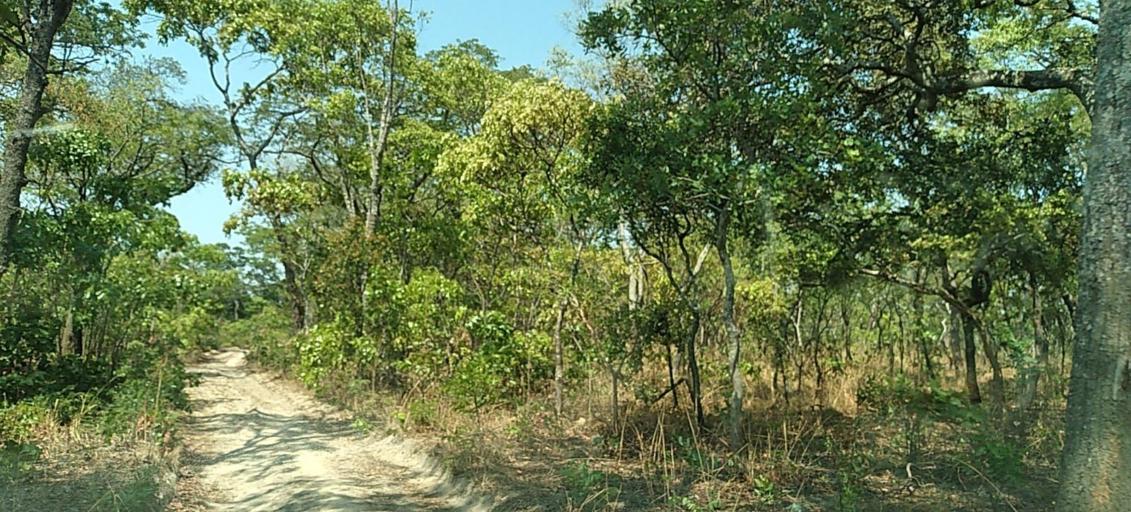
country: ZM
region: Copperbelt
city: Mpongwe
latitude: -13.7907
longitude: 28.0927
